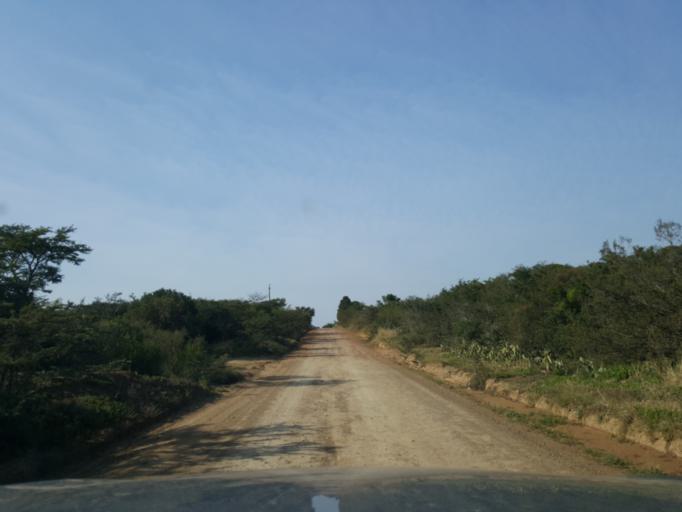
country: ZA
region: Eastern Cape
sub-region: Cacadu District Municipality
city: Grahamstown
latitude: -33.4128
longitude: 26.3106
